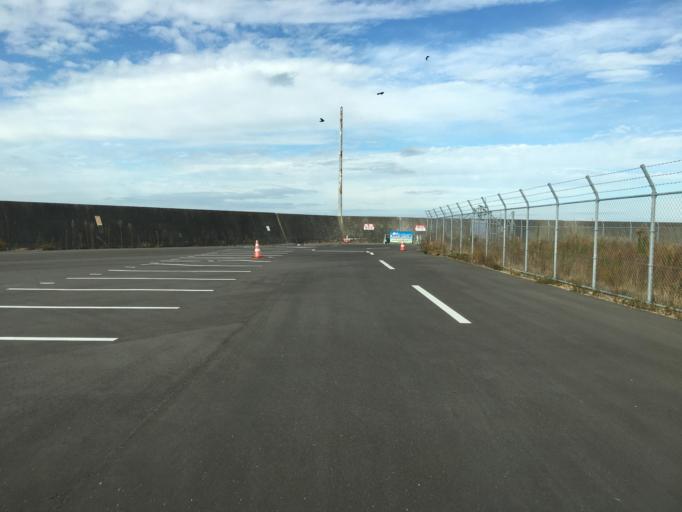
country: JP
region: Miyagi
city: Marumori
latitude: 37.8577
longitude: 140.9499
